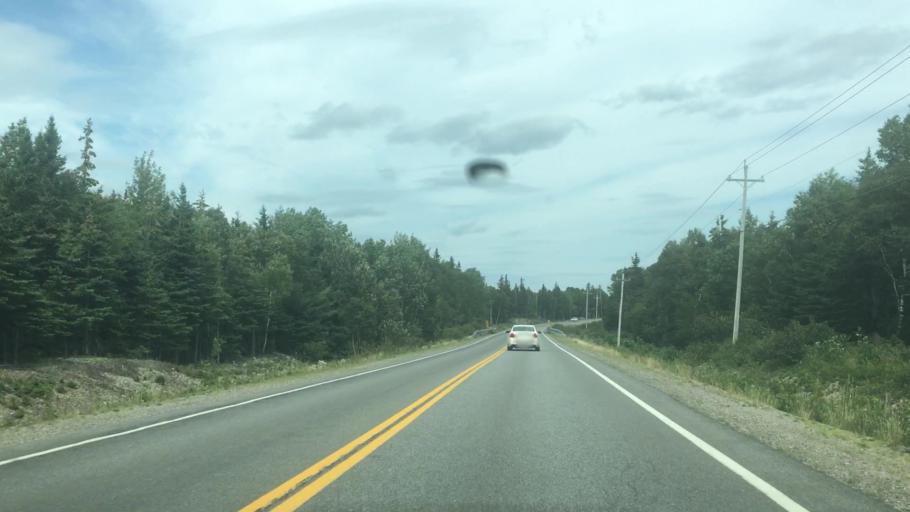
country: CA
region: Nova Scotia
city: Sydney Mines
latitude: 46.5122
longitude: -60.4304
